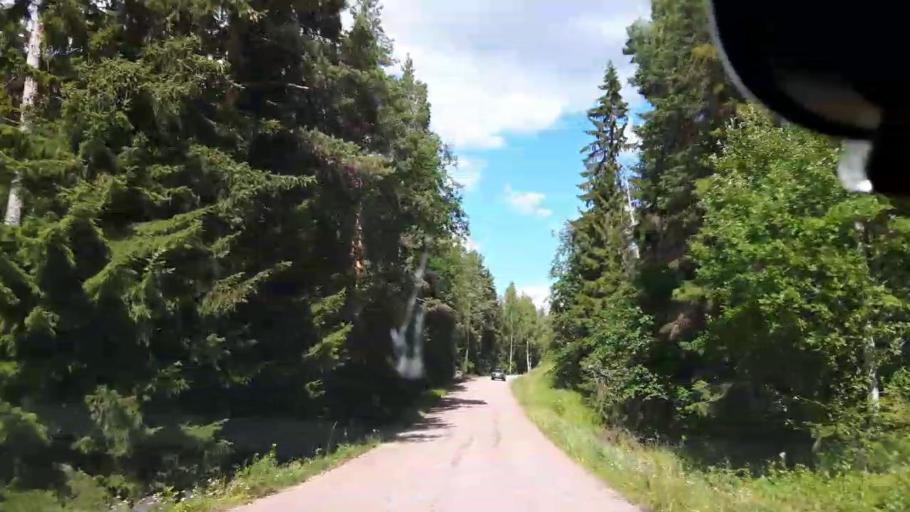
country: SE
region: Jaemtland
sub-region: Ragunda Kommun
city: Hammarstrand
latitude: 62.9382
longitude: 16.6919
